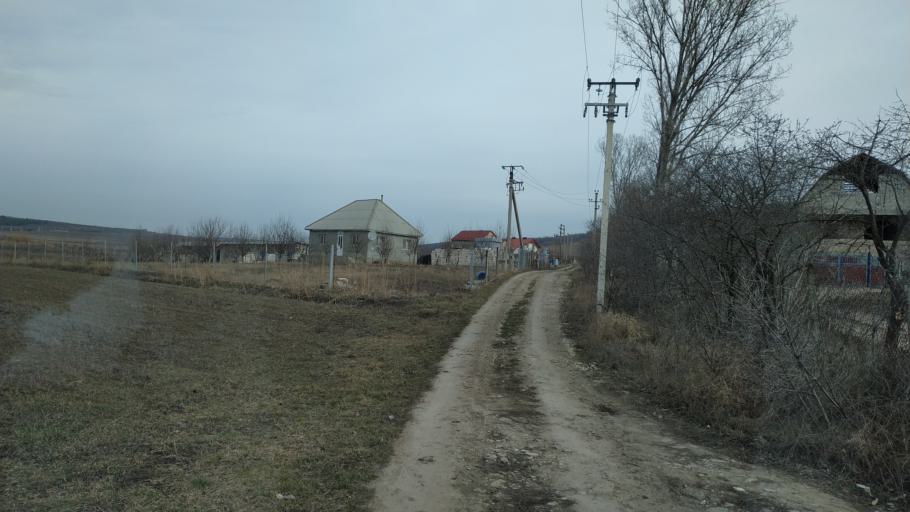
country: MD
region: Chisinau
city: Vatra
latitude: 47.0980
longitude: 28.7362
